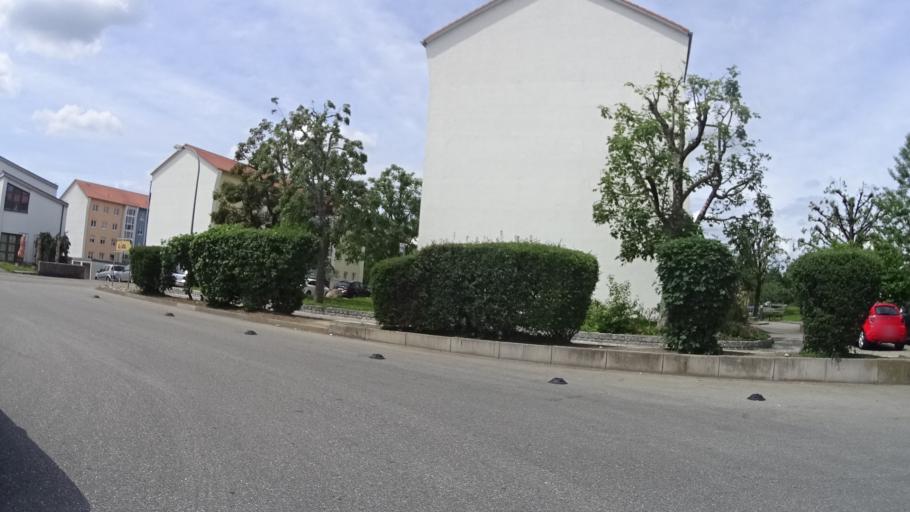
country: DE
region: Baden-Wuerttemberg
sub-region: Freiburg Region
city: Rheinfelden (Baden)
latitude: 47.5578
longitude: 7.7812
